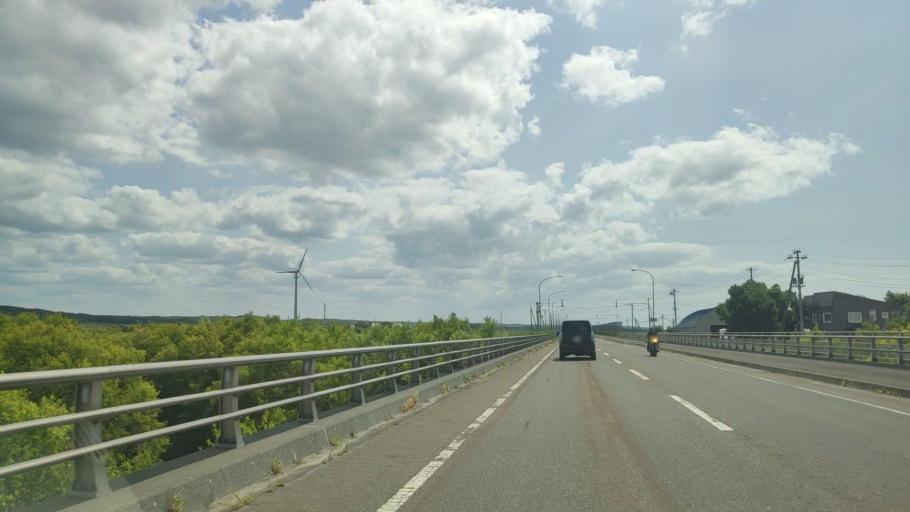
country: JP
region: Hokkaido
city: Makubetsu
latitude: 44.7538
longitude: 141.7950
